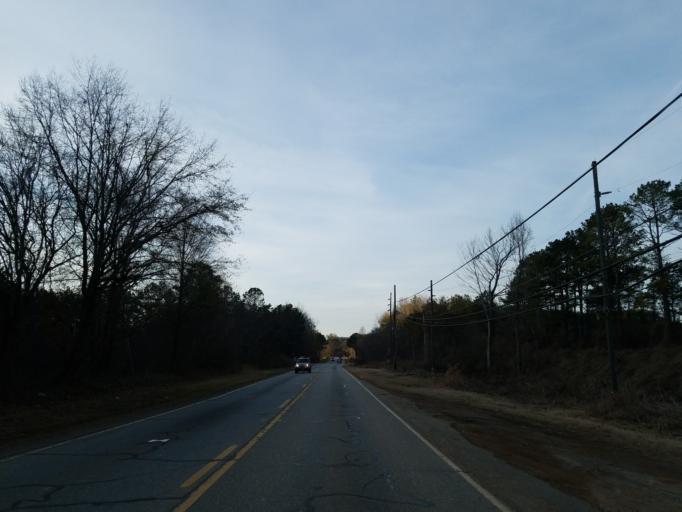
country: US
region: Georgia
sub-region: Bartow County
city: Emerson
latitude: 34.1441
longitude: -84.7679
